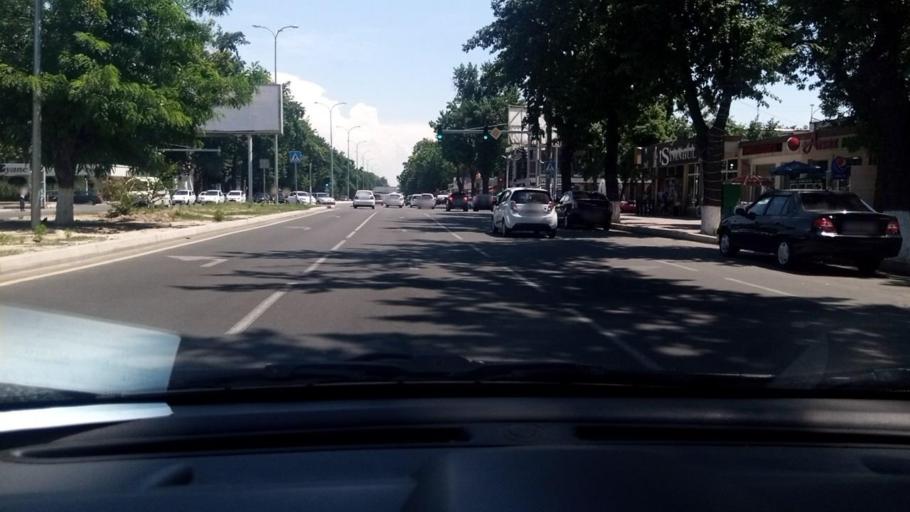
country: UZ
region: Toshkent Shahri
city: Tashkent
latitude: 41.2869
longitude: 69.2048
